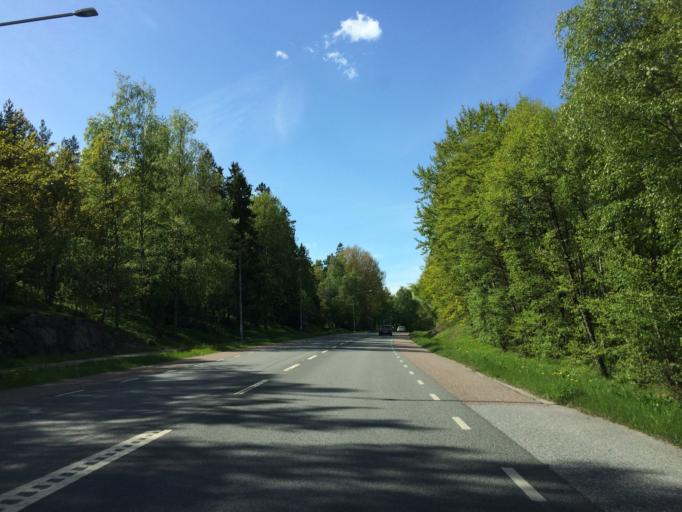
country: SE
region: Stockholm
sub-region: Norrtalje Kommun
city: Bergshamra
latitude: 59.4167
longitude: 18.0123
